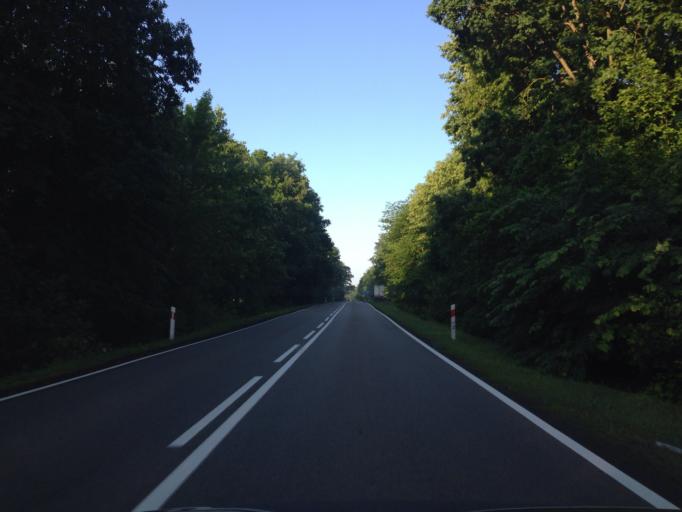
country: PL
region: Pomeranian Voivodeship
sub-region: Powiat kwidzynski
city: Gardeja
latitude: 53.5883
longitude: 18.9087
